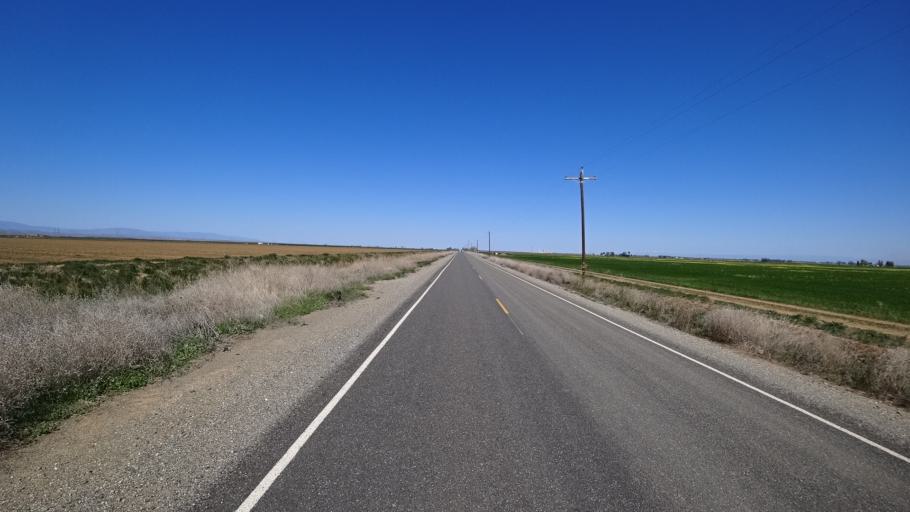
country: US
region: California
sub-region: Glenn County
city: Willows
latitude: 39.4806
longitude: -122.2490
